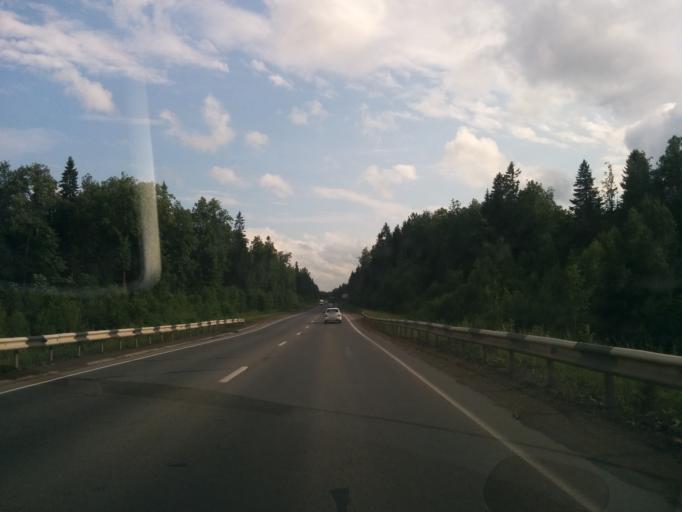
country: RU
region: Perm
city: Polazna
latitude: 58.1094
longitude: 56.4261
